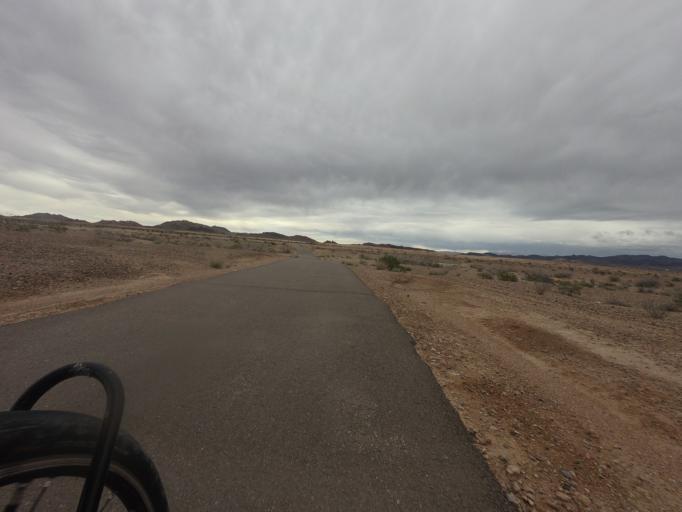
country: US
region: Nevada
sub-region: Clark County
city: Henderson
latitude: 36.1033
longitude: -115.0014
